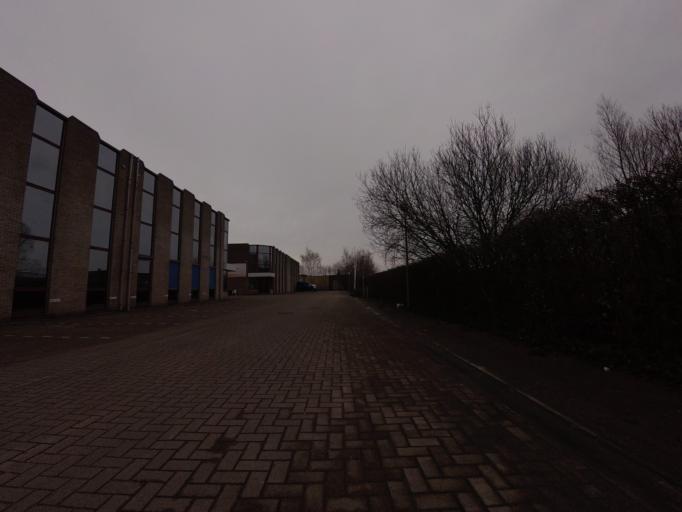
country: BE
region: Flanders
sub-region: Provincie Antwerpen
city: Aartselaar
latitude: 51.1197
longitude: 4.3704
